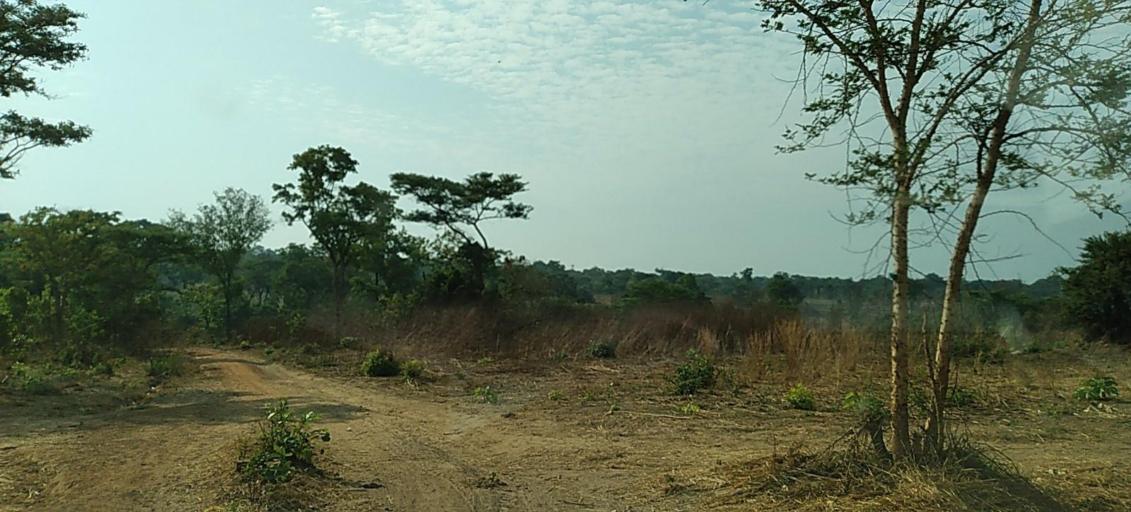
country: ZM
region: Copperbelt
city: Kalulushi
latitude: -13.0067
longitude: 27.7182
